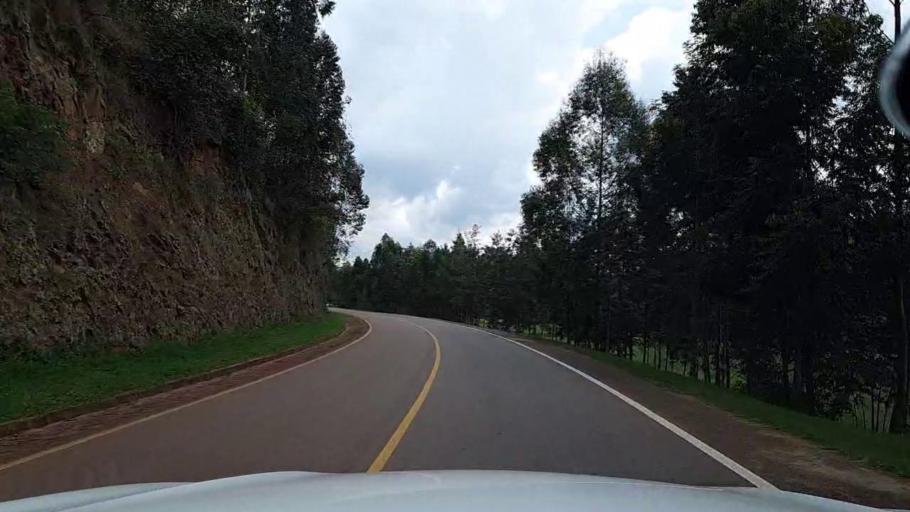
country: RW
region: Kigali
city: Kigali
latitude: -1.8177
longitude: 30.1171
